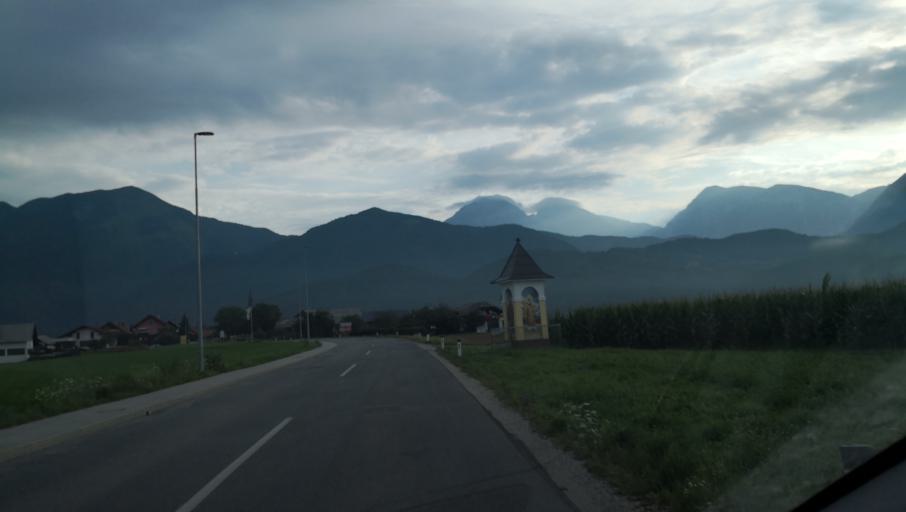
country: SI
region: Preddvor
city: Preddvor
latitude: 46.2777
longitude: 14.4208
